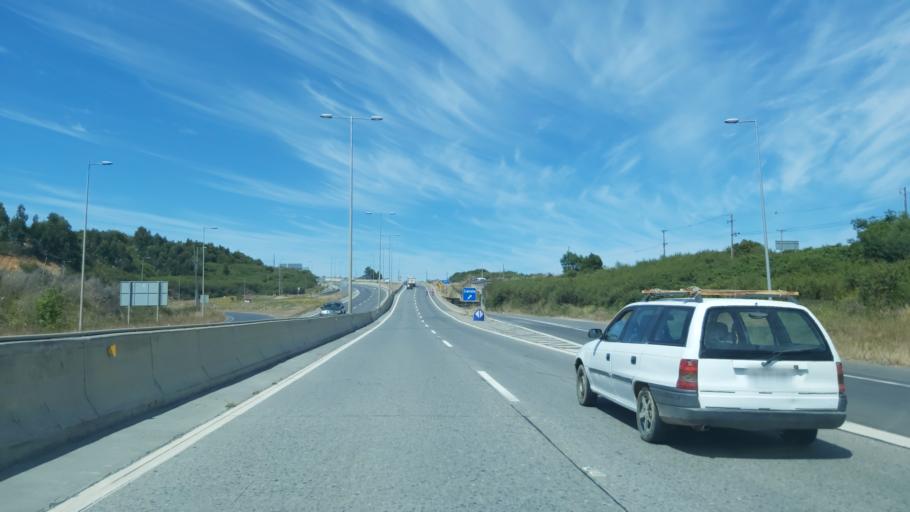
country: CL
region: Biobio
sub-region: Provincia de Concepcion
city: Coronel
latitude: -37.0441
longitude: -73.1400
